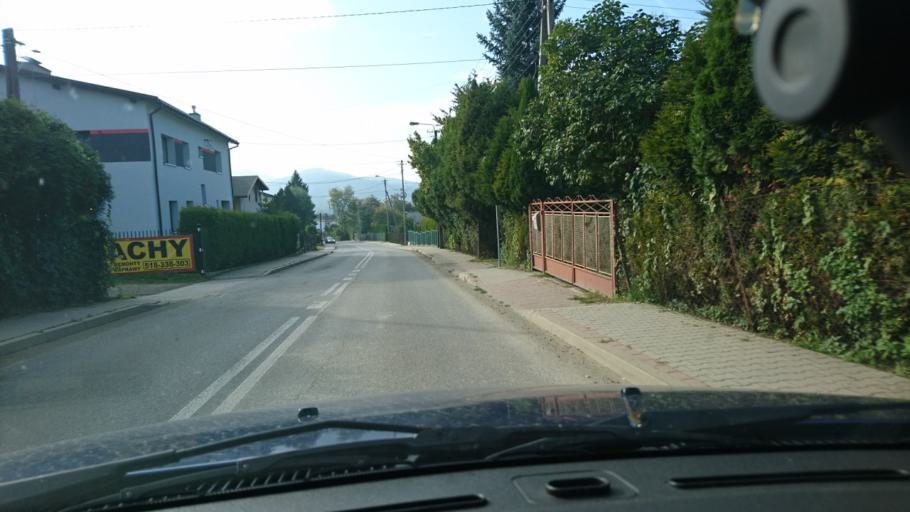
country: PL
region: Silesian Voivodeship
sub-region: Powiat bielski
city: Wilkowice
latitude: 49.7604
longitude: 19.1010
